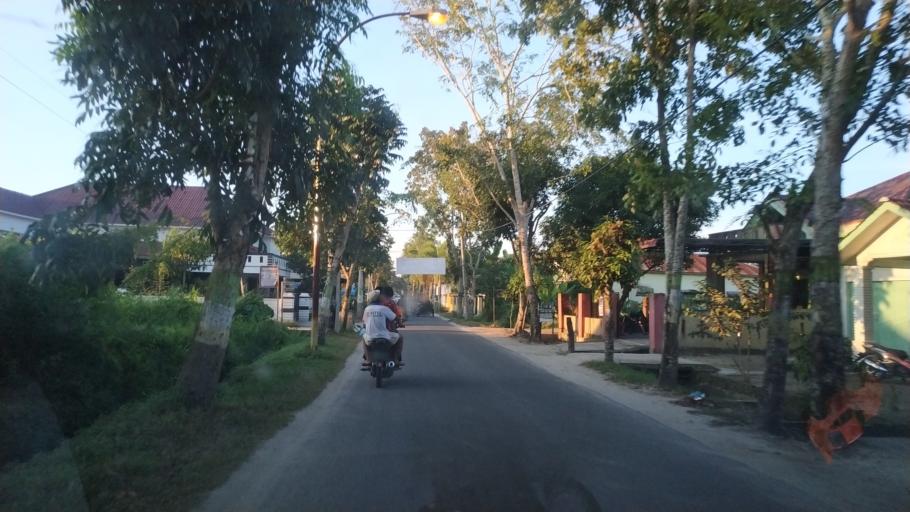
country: ID
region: North Sumatra
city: Tanjungbalai
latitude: 2.9468
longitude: 99.7879
